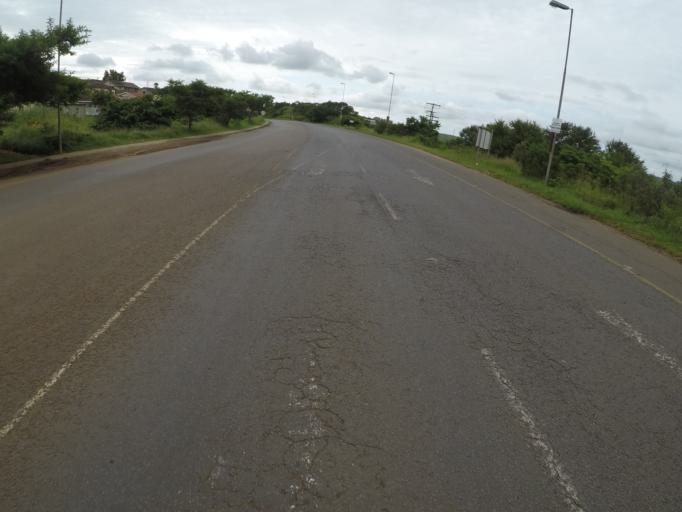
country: ZA
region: KwaZulu-Natal
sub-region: uThungulu District Municipality
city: Empangeni
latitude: -28.7771
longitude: 31.8766
